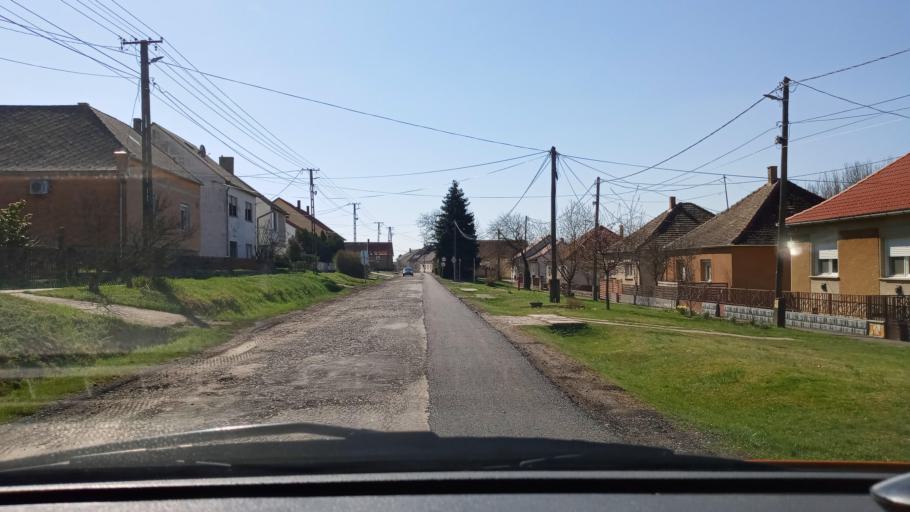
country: HU
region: Baranya
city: Boly
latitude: 46.0137
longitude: 18.4121
